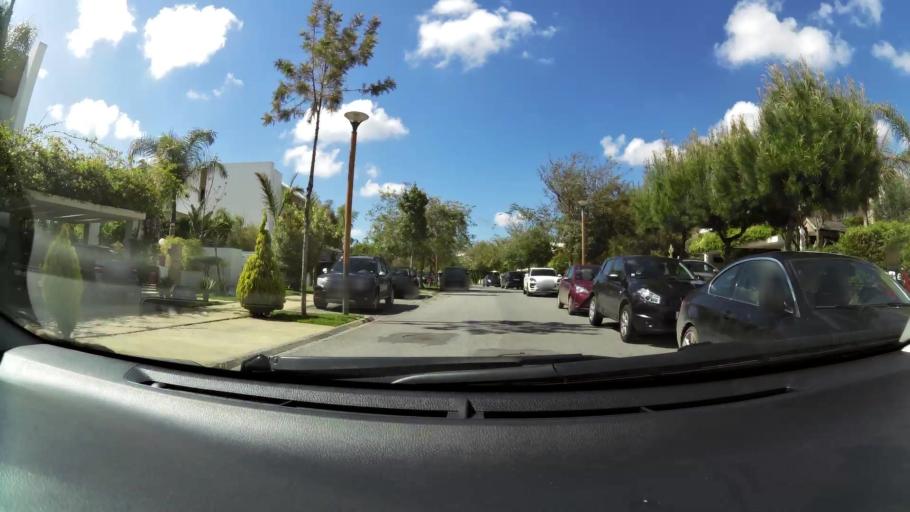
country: MA
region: Grand Casablanca
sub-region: Nouaceur
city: Bouskoura
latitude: 33.4939
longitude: -7.5972
